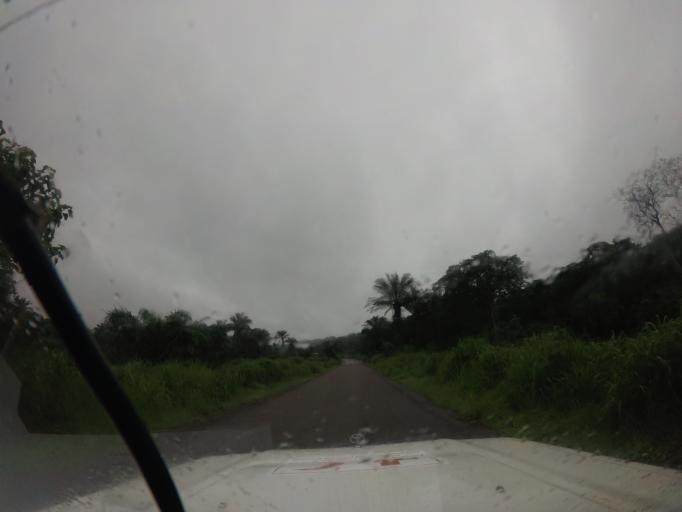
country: SL
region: Northern Province
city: Kabala
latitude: 9.4689
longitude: -11.6736
